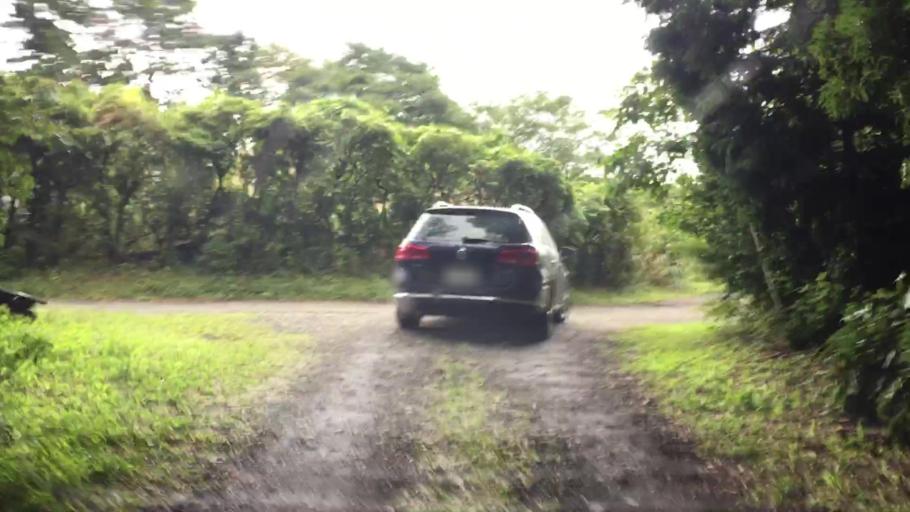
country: JP
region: Yamanashi
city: Fujikawaguchiko
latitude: 35.4055
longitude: 138.5667
